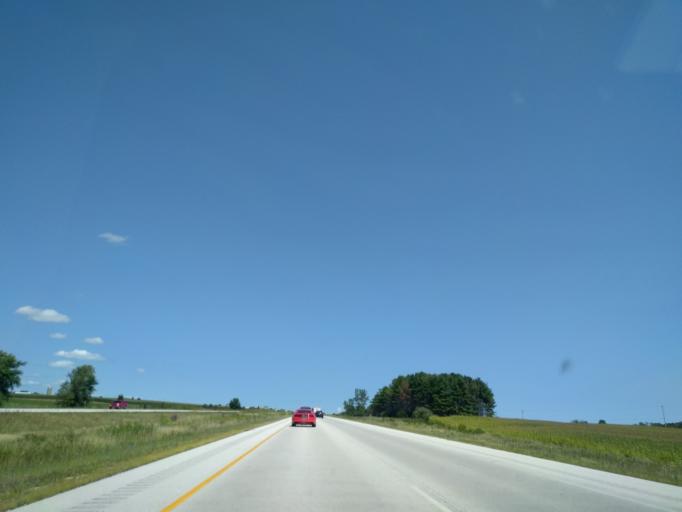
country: US
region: Wisconsin
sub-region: Sheboygan County
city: Cedar Grove
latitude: 43.5782
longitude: -87.7930
